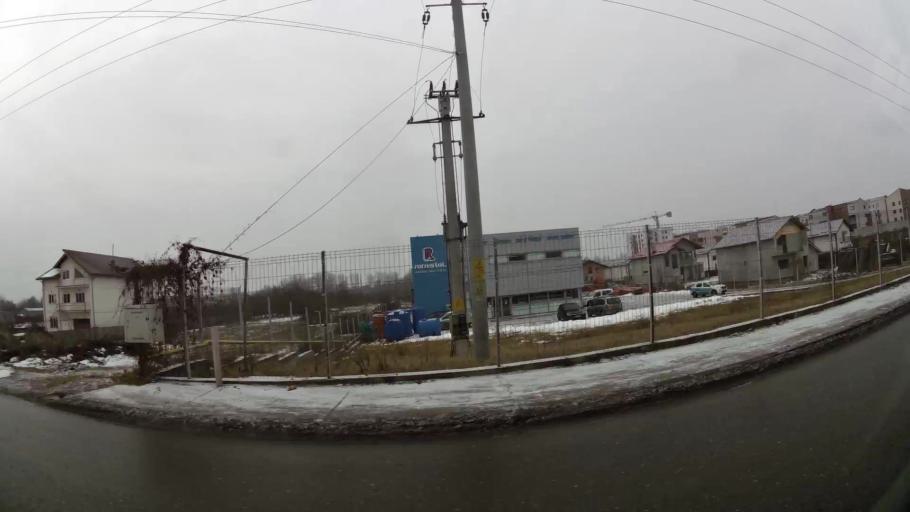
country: RO
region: Dambovita
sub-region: Municipiul Targoviste
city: Targoviste
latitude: 44.9400
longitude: 25.4640
